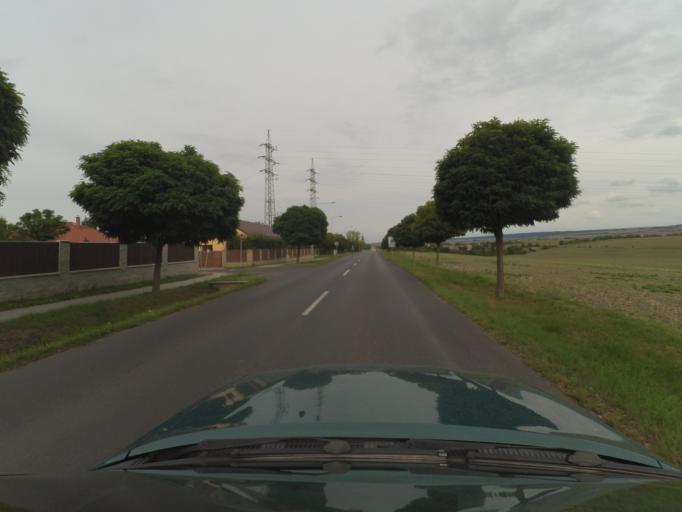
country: CZ
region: Ustecky
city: Cerncice
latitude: 50.3602
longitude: 13.8337
